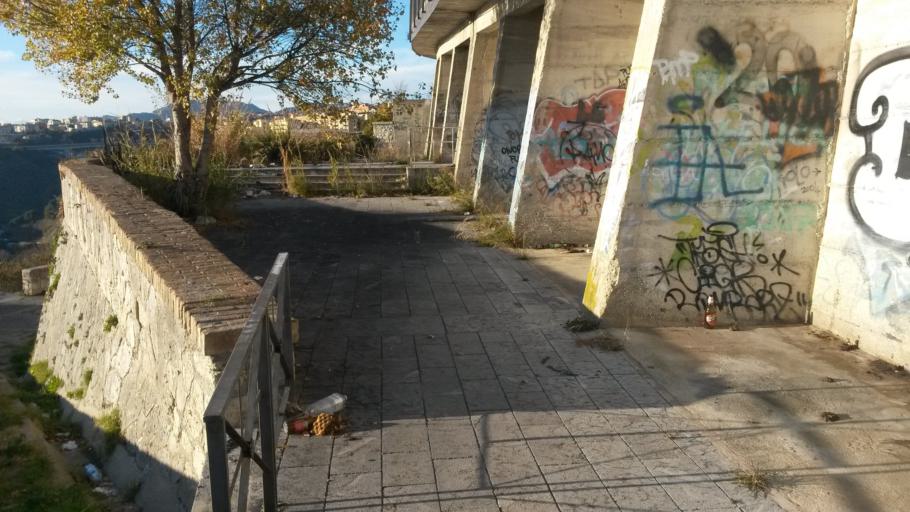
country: IT
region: Calabria
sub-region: Provincia di Catanzaro
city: Siano
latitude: 38.9084
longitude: 16.5877
